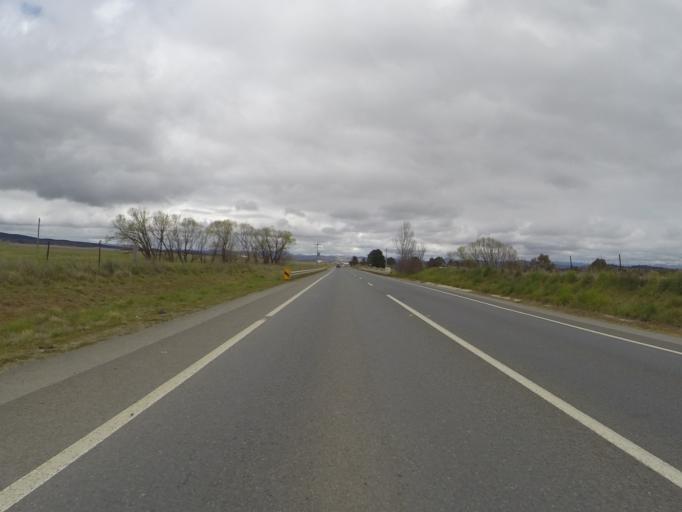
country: AU
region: Australian Capital Territory
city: Canberra
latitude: -35.2686
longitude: 149.1963
